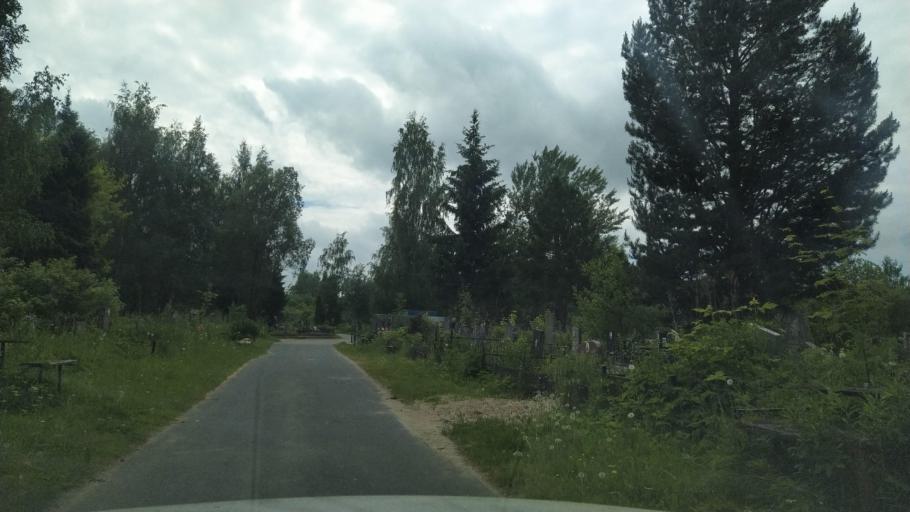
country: RU
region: St.-Petersburg
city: Pushkin
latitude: 59.6925
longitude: 30.3818
